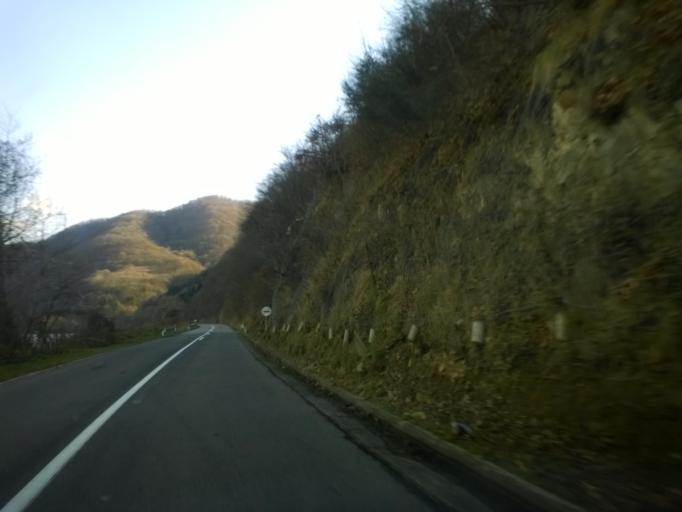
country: RS
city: Radenka
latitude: 44.6487
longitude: 21.8068
